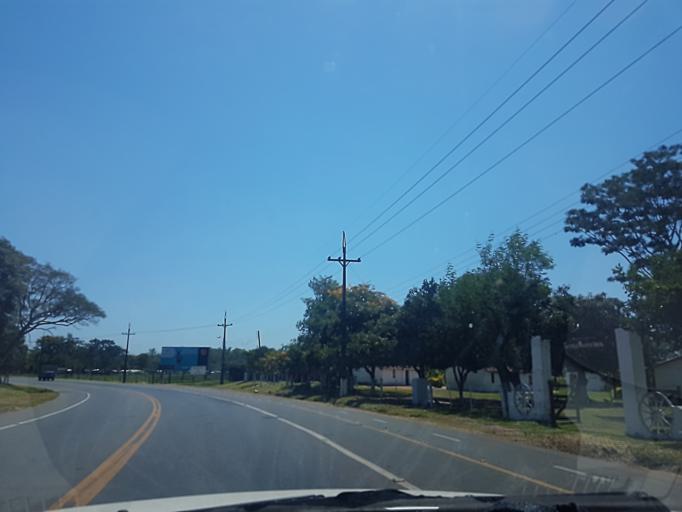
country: PY
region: Central
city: Aregua
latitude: -25.2379
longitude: -57.4228
